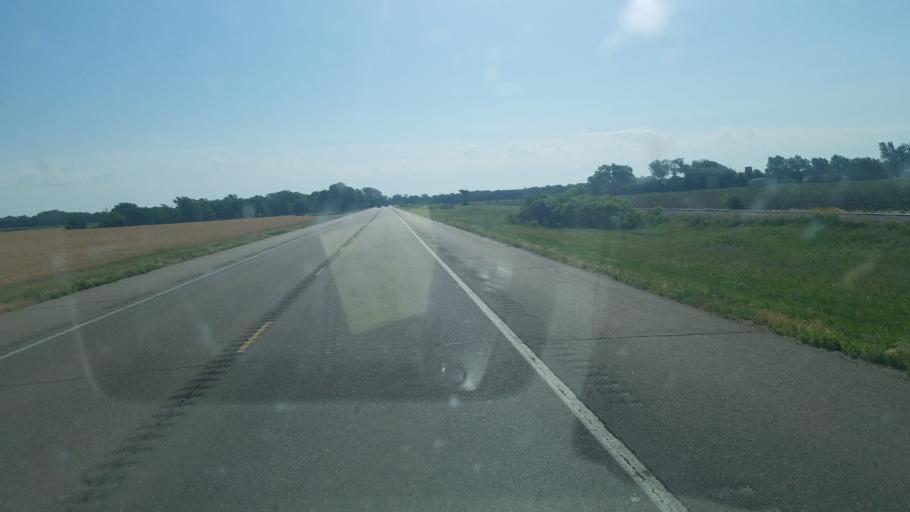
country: US
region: Kansas
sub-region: Barton County
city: Great Bend
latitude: 38.3634
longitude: -98.7278
